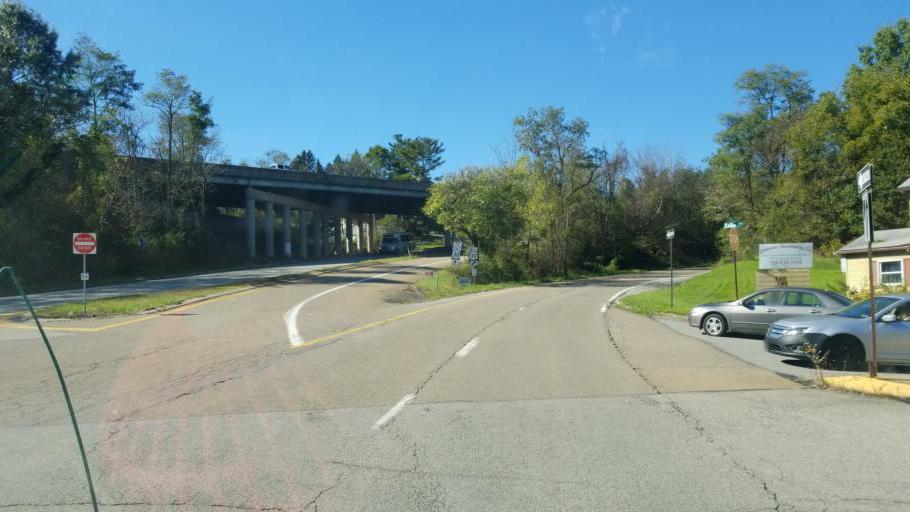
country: US
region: Pennsylvania
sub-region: Westmoreland County
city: Southwest Greensburg
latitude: 40.3034
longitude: -79.5618
